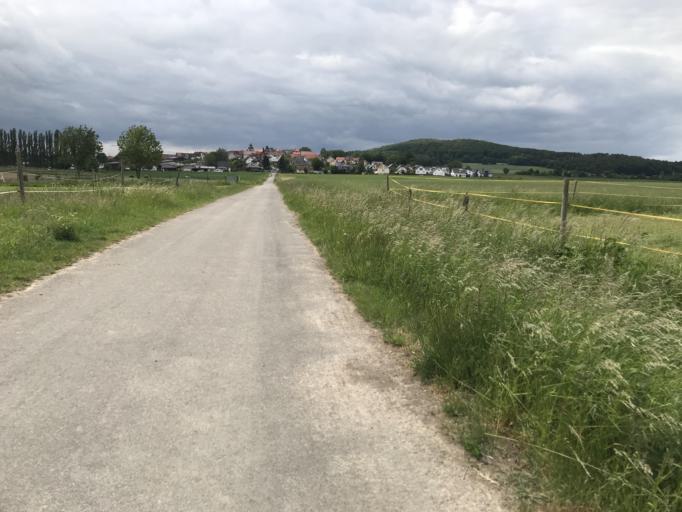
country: DE
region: Hesse
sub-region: Regierungsbezirk Kassel
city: Martinhagen
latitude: 51.2857
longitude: 9.2986
